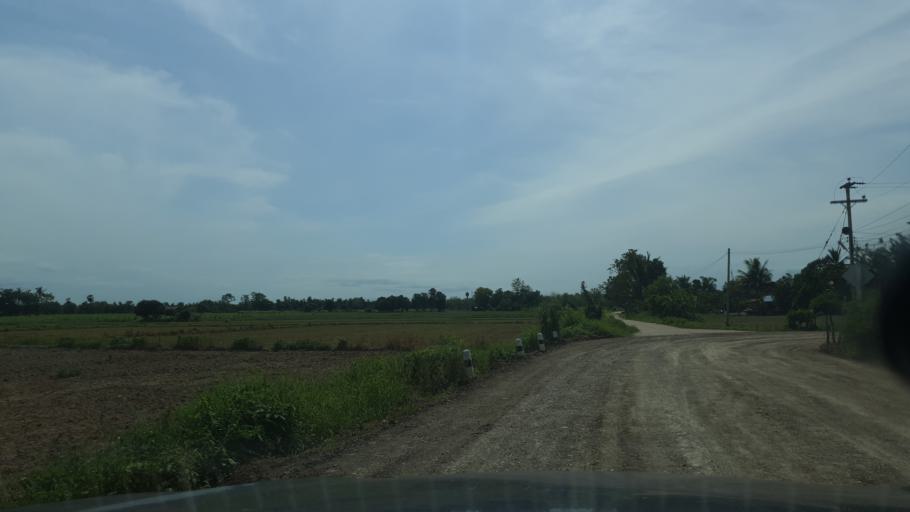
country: TH
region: Sukhothai
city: Si Samrong
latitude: 17.2079
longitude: 99.7201
